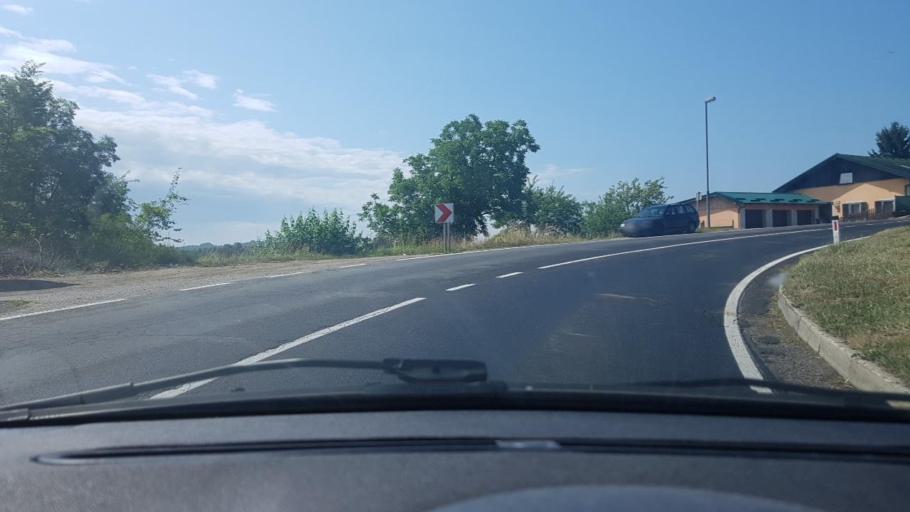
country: SI
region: Sentilj
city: Sentilj v Slov. Goricah
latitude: 46.6836
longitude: 15.6638
